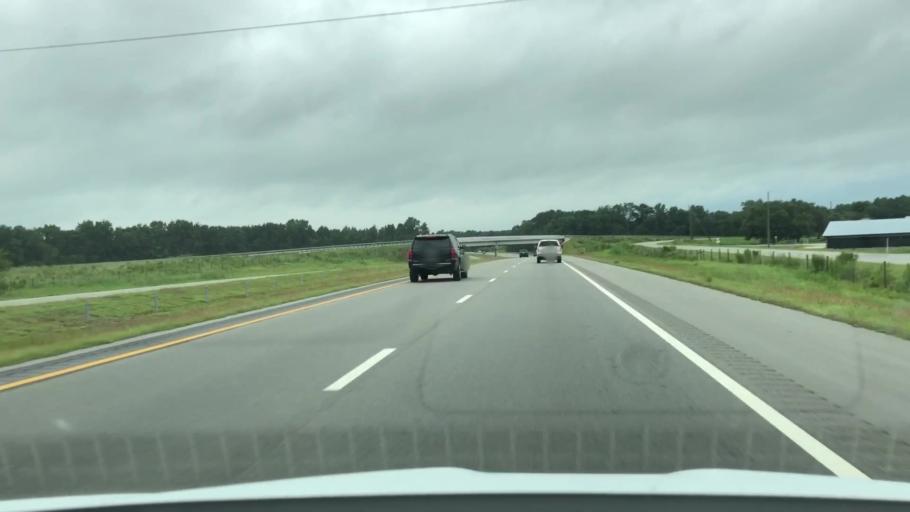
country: US
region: North Carolina
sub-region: Wayne County
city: Elroy
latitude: 35.3529
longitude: -77.8480
